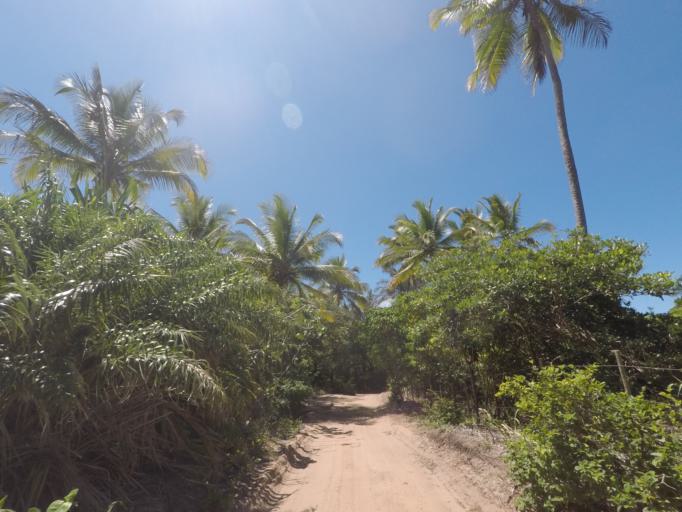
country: BR
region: Bahia
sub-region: Marau
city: Marau
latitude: -14.0147
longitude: -38.9440
